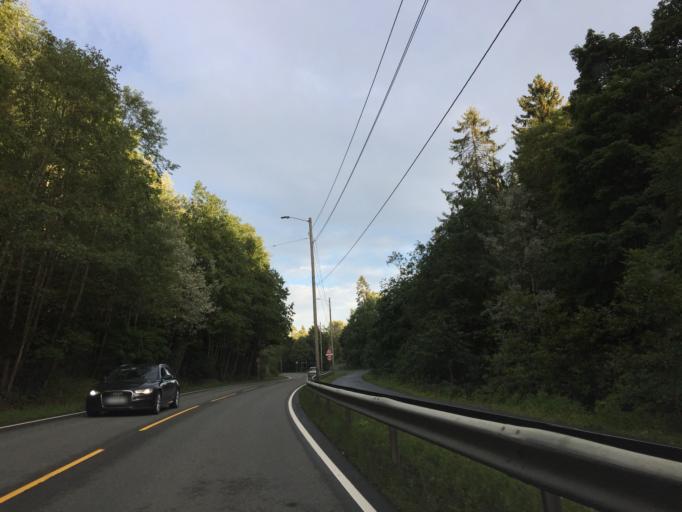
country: NO
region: Akershus
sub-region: Oppegard
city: Kolbotn
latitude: 59.8415
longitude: 10.8266
